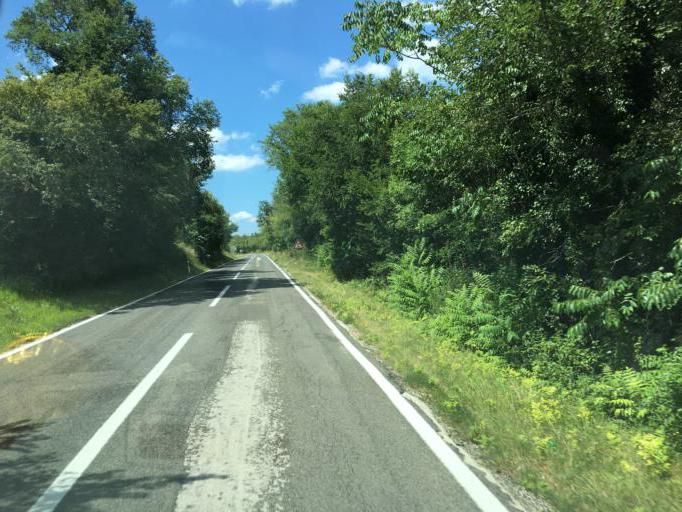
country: HR
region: Istarska
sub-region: Grad Rovinj
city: Rovinj
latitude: 45.1458
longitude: 13.7317
